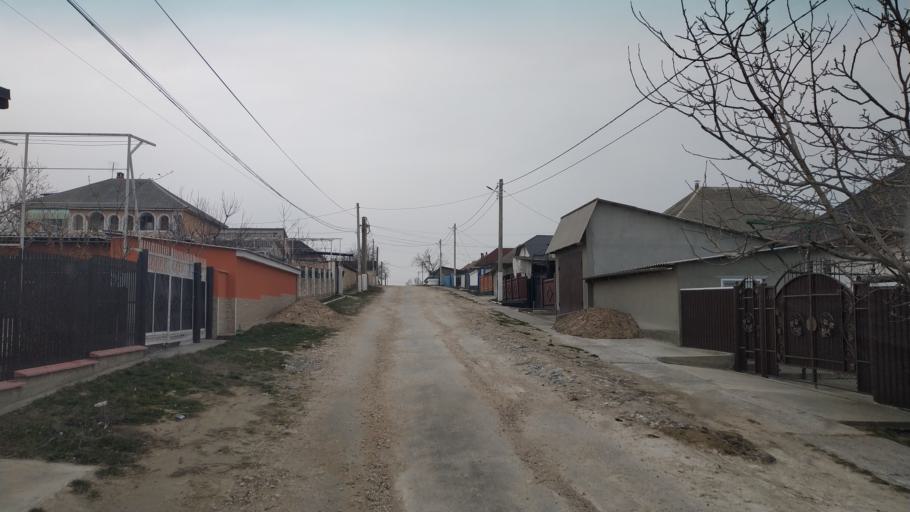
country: MD
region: Chisinau
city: Singera
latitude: 46.8239
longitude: 28.9648
